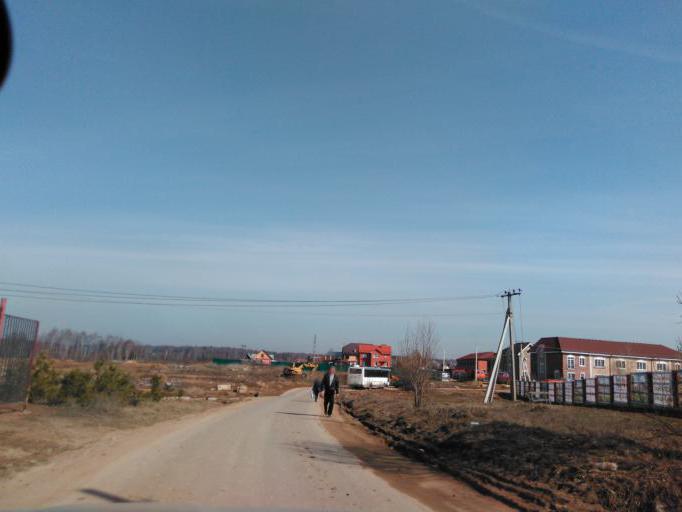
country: RU
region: Moskovskaya
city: Opalikha
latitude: 55.8770
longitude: 37.2582
